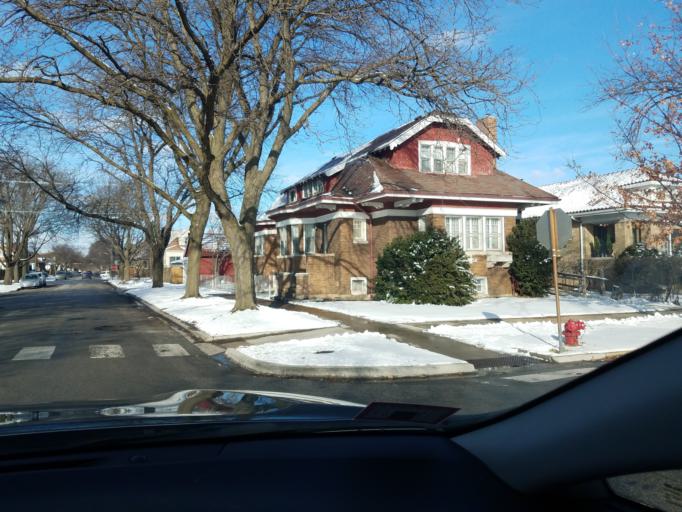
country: US
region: Illinois
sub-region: Cook County
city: Harwood Heights
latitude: 41.9578
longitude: -87.7622
